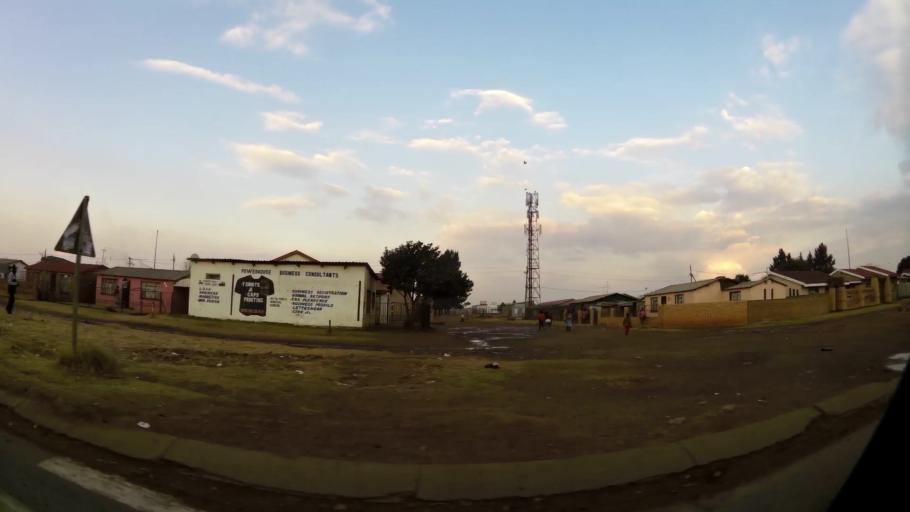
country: ZA
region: Gauteng
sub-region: City of Johannesburg Metropolitan Municipality
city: Orange Farm
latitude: -26.5591
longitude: 27.8384
